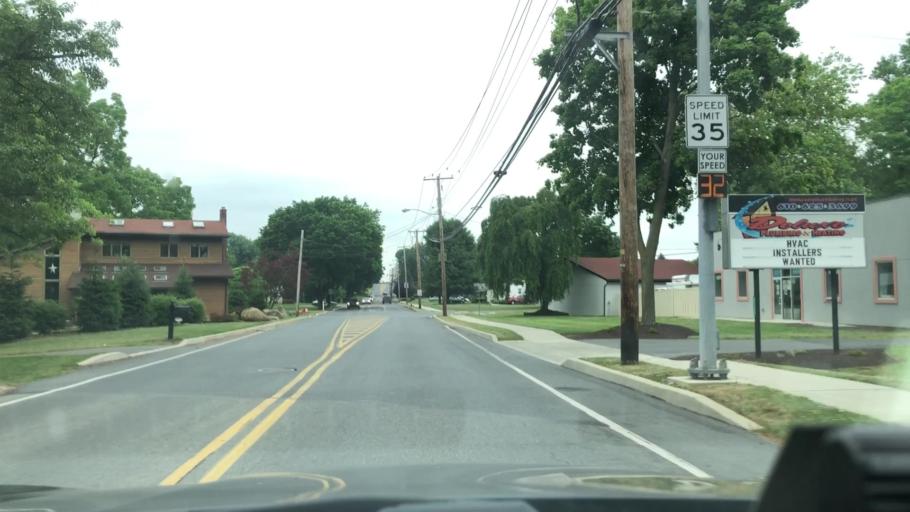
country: US
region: Pennsylvania
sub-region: Northampton County
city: Bethlehem
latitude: 40.6476
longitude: -75.3992
